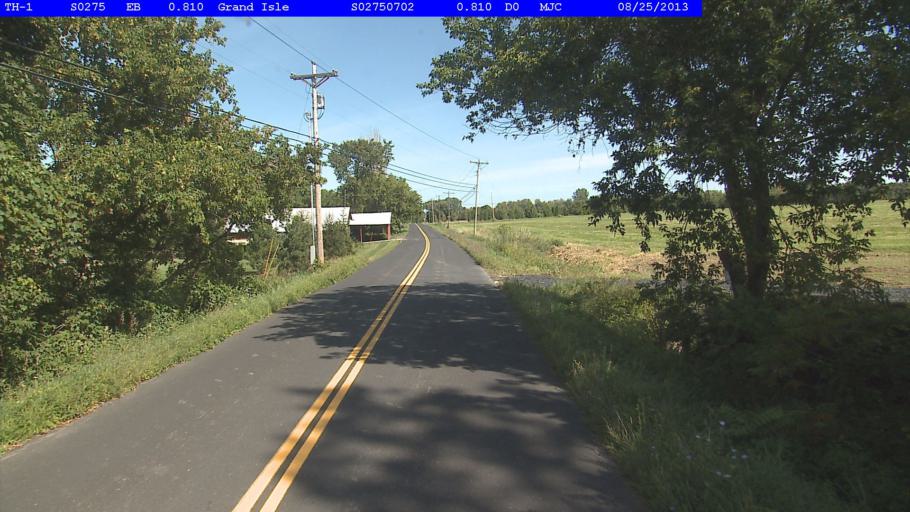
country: US
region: New York
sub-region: Clinton County
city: Cumberland Head
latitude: 44.7120
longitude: -73.3422
